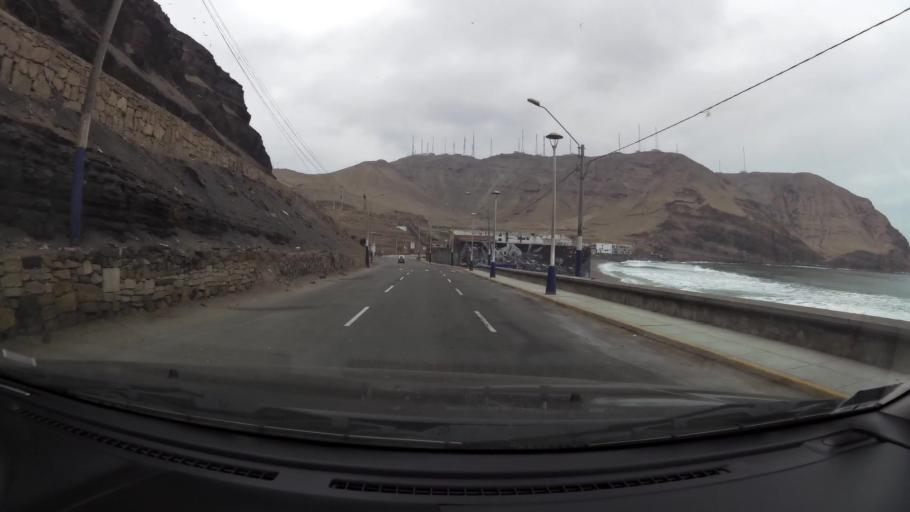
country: PE
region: Lima
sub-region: Lima
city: Surco
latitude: -12.1724
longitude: -77.0344
